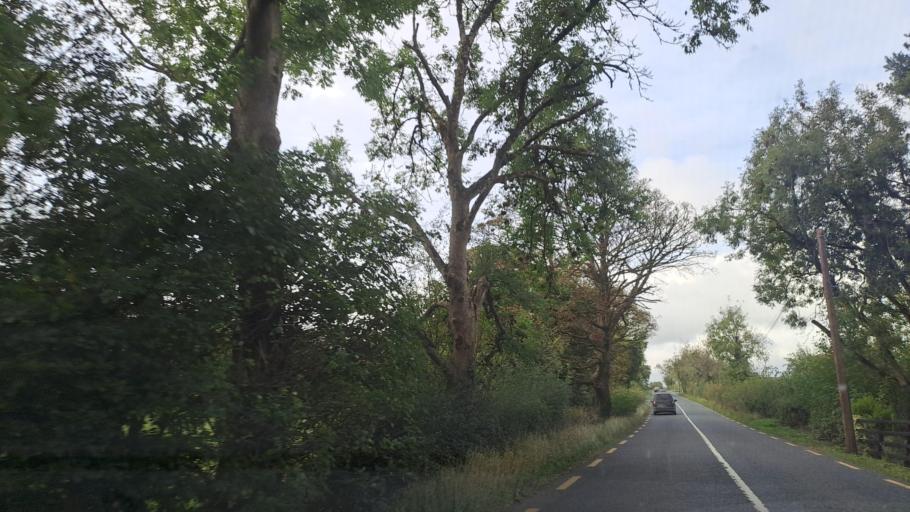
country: IE
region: Ulster
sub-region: An Cabhan
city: Kingscourt
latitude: 53.8439
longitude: -6.7733
